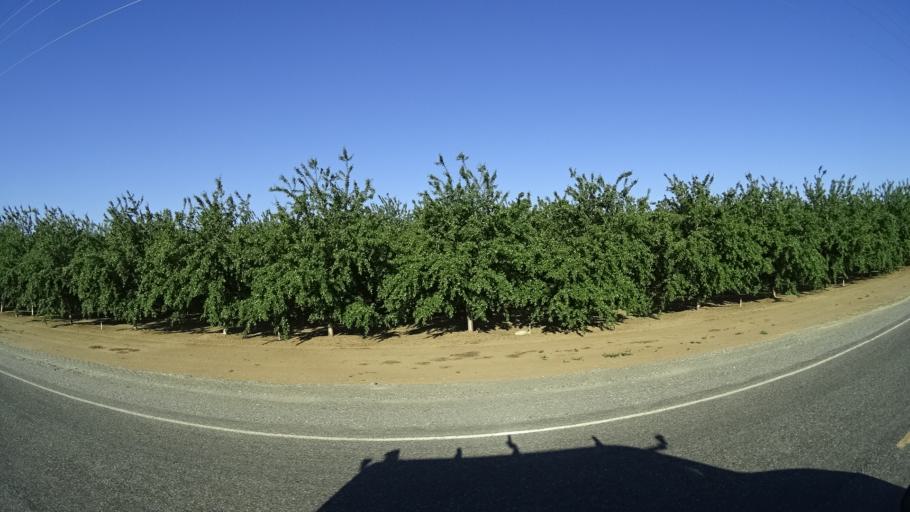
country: US
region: California
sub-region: Glenn County
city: Orland
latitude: 39.7027
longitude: -122.1781
